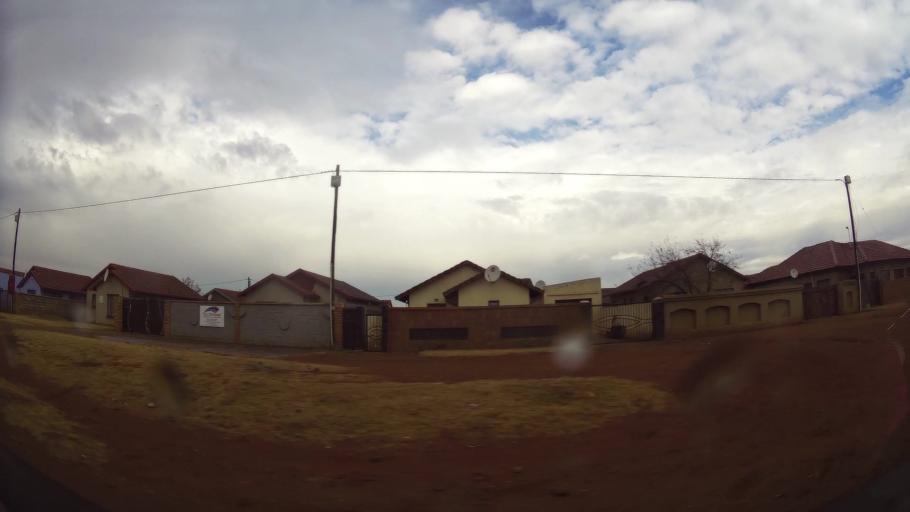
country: ZA
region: Gauteng
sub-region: Ekurhuleni Metropolitan Municipality
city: Germiston
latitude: -26.3321
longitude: 28.2062
